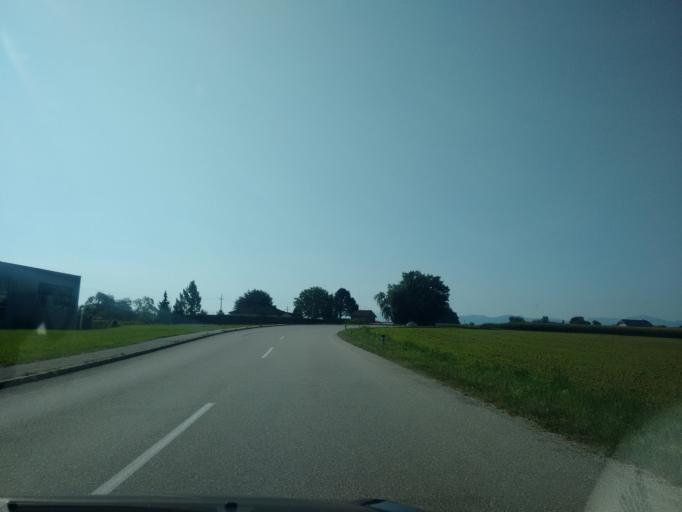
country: AT
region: Upper Austria
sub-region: Wels-Land
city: Sattledt
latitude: 48.0164
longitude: 14.0646
